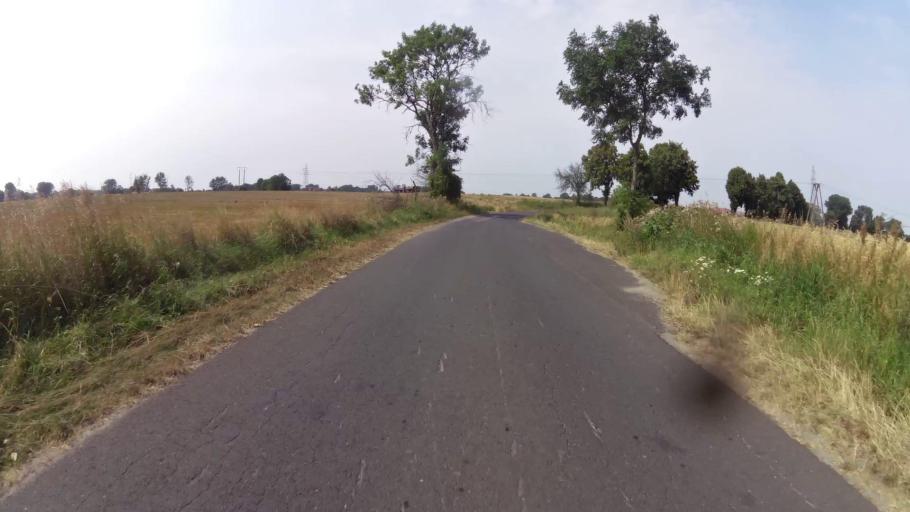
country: PL
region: West Pomeranian Voivodeship
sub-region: Powiat mysliborski
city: Nowogrodek Pomorski
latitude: 52.9721
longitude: 15.0222
